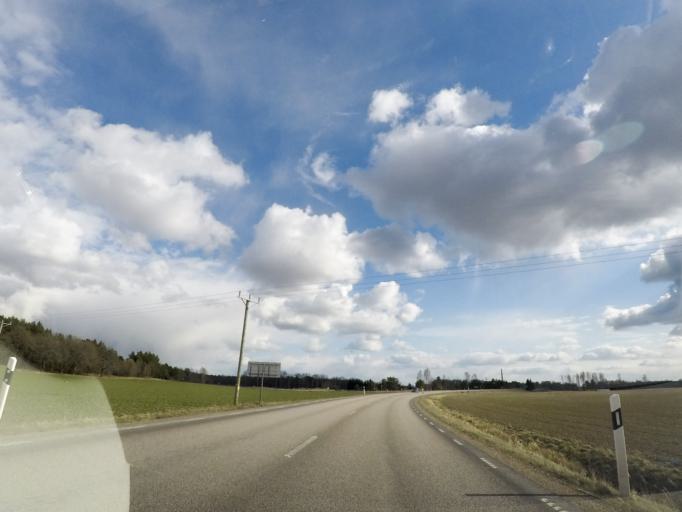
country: SE
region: Vaestmanland
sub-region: Hallstahammars Kommun
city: Hallstahammar
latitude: 59.5926
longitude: 16.2152
